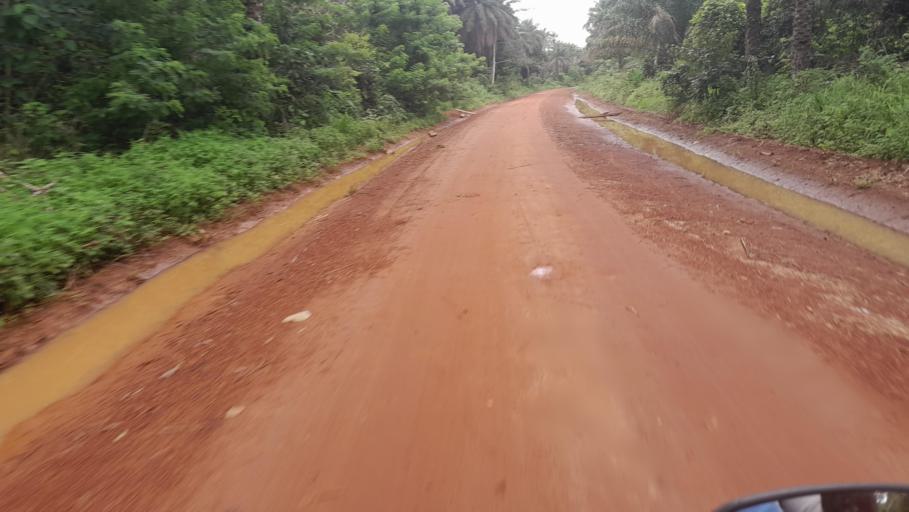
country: GN
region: Boke
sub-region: Boffa
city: Boffa
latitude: 10.0497
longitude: -13.8731
